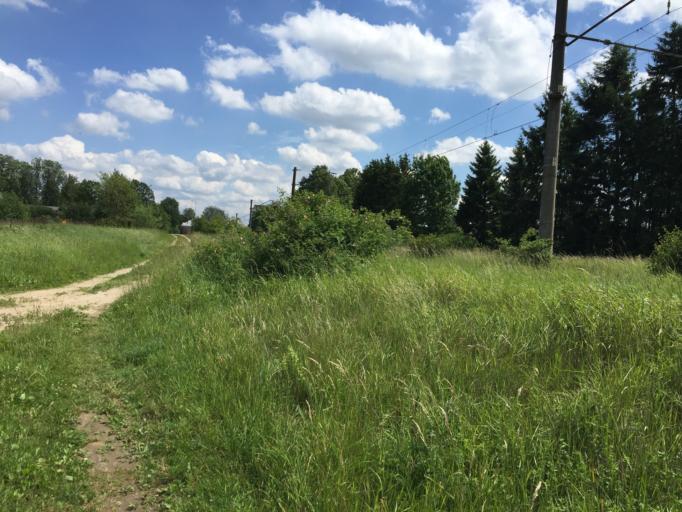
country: LV
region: Engure
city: Smarde
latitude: 56.9570
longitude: 23.3314
